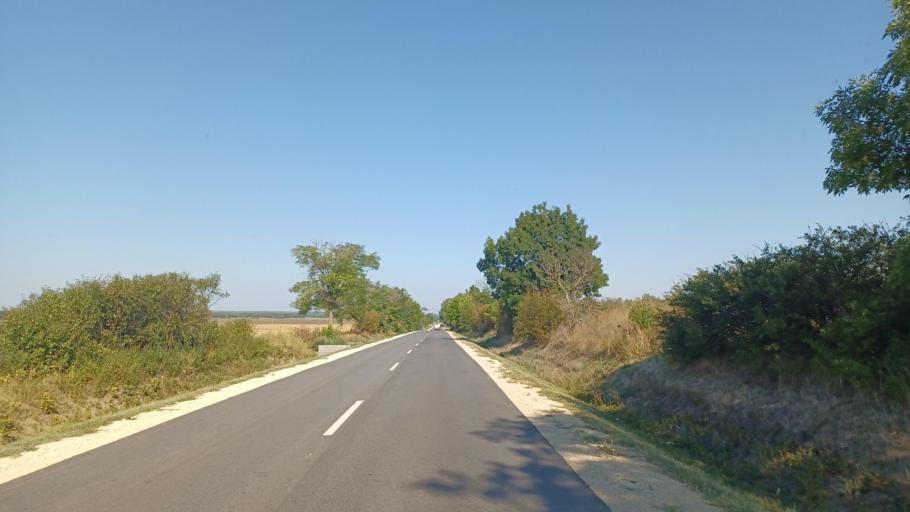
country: HU
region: Tolna
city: Paks
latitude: 46.6522
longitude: 18.8390
